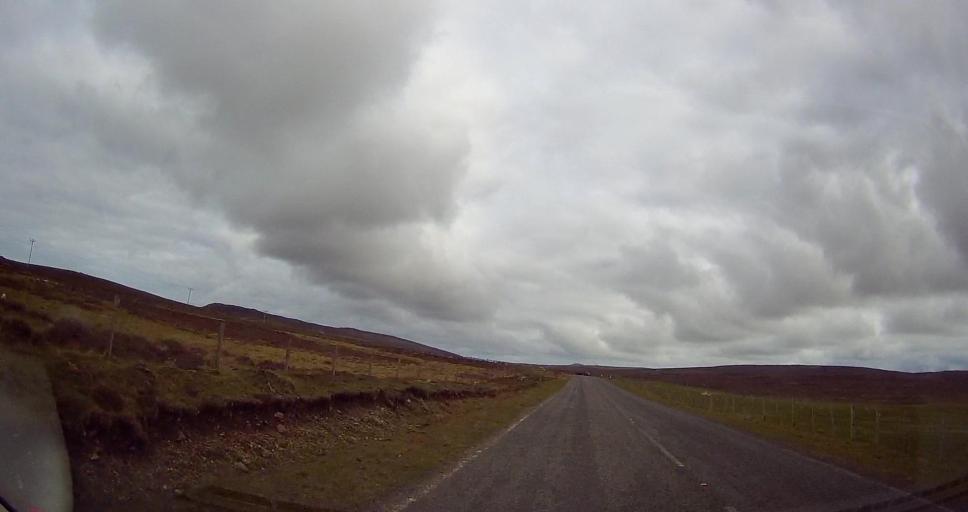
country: GB
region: Scotland
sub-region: Shetland Islands
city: Shetland
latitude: 60.6983
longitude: -0.9216
